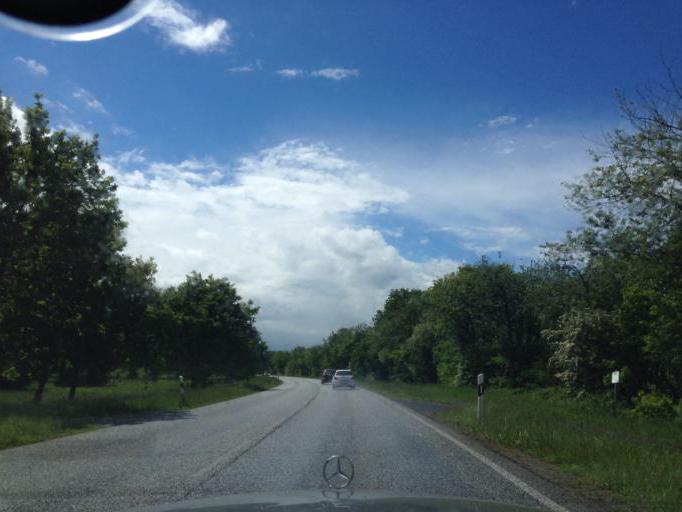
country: DE
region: Schleswig-Holstein
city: Norderstedt
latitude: 53.6985
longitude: 10.0108
